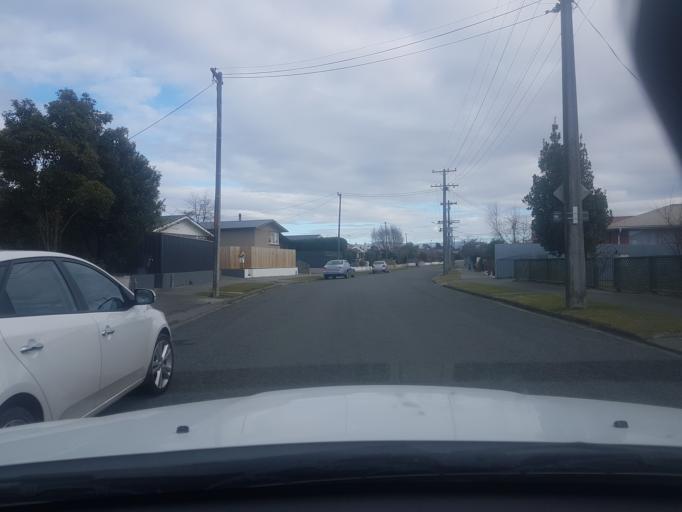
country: NZ
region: Canterbury
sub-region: Timaru District
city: Timaru
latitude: -44.3902
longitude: 171.2123
